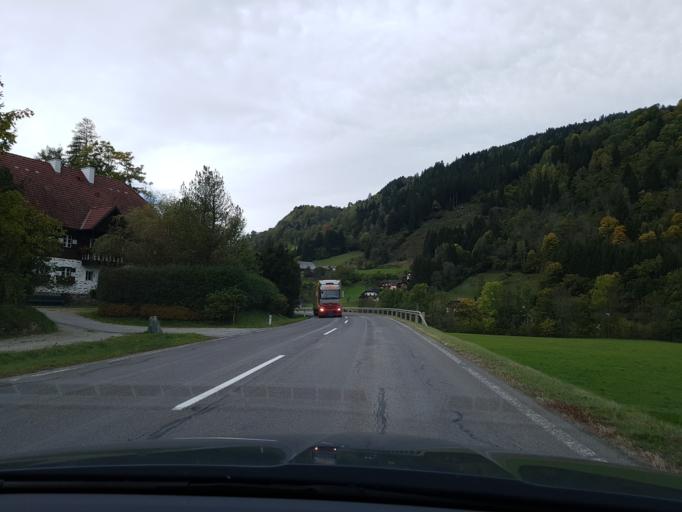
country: AT
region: Styria
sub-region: Politischer Bezirk Murau
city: Stadl an der Mur
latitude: 47.0698
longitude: 13.9104
